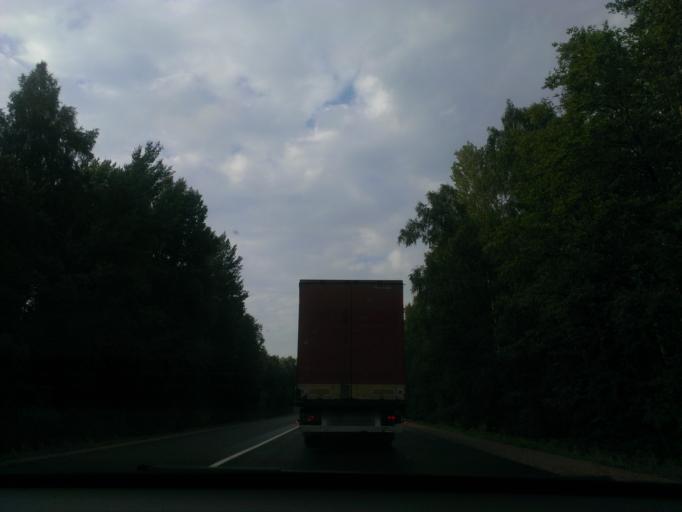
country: LV
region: Lecava
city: Iecava
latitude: 56.6636
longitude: 24.2331
